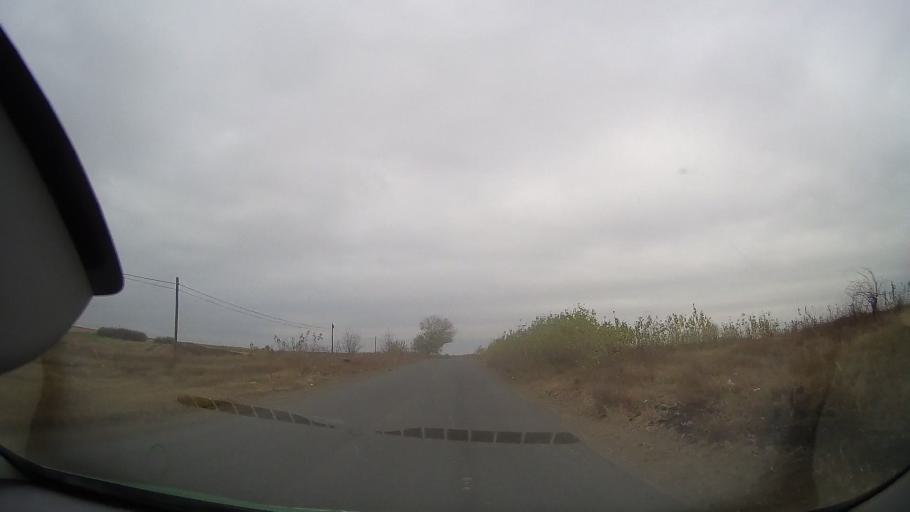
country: RO
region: Braila
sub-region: Comuna Ulmu
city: Ulmu
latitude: 44.9530
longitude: 27.2973
